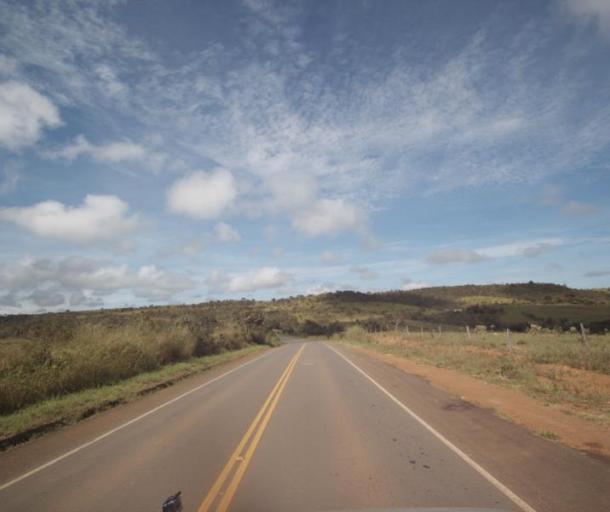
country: BR
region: Goias
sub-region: Pirenopolis
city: Pirenopolis
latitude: -16.0042
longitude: -48.8415
